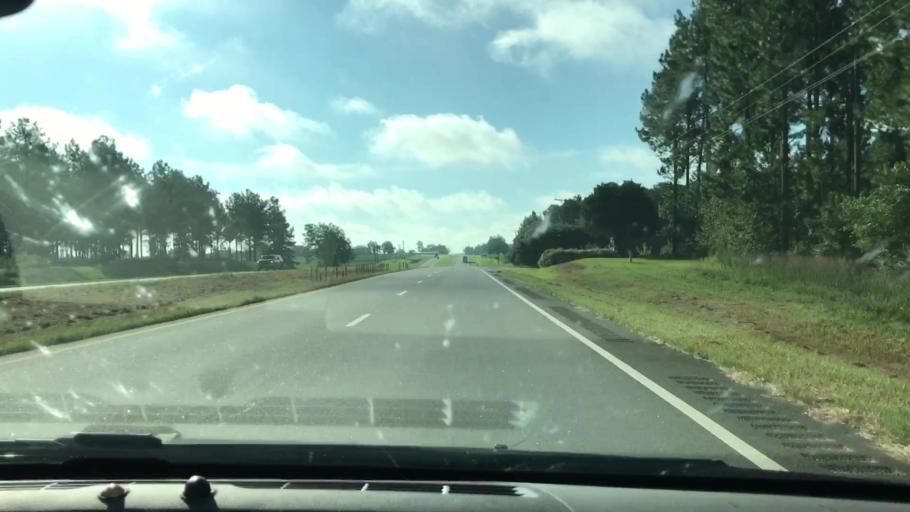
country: US
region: Georgia
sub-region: Terrell County
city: Dawson
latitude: 31.7411
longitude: -84.4112
